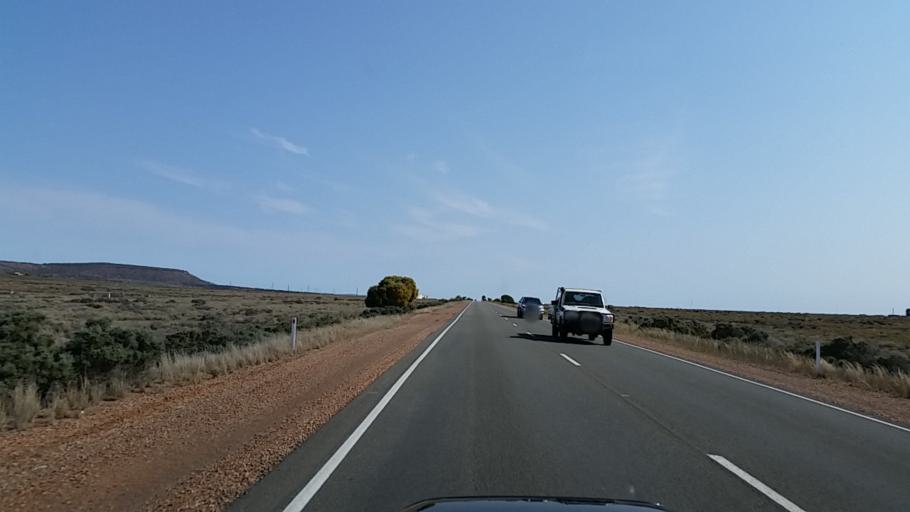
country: AU
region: South Australia
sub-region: Port Augusta
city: Port Augusta West
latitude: -32.6058
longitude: 137.5877
